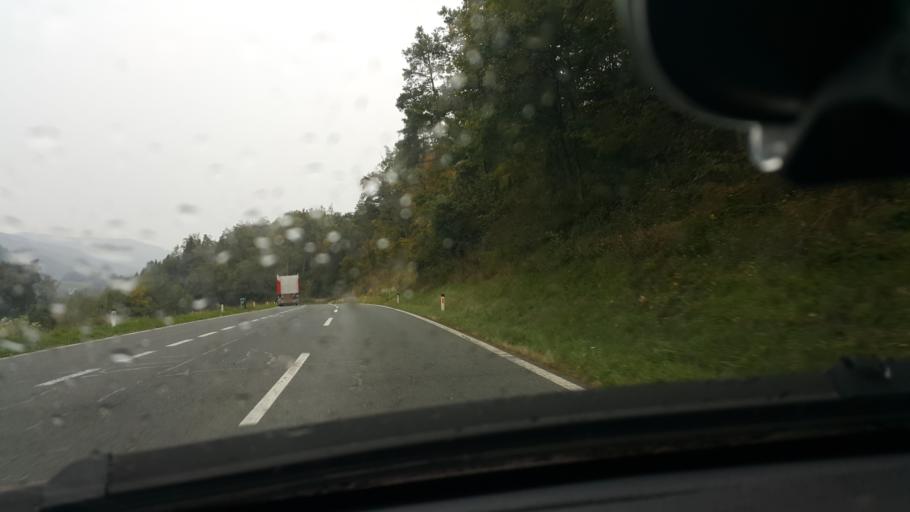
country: SI
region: Dravograd
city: Dravograd
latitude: 46.6064
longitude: 14.9824
